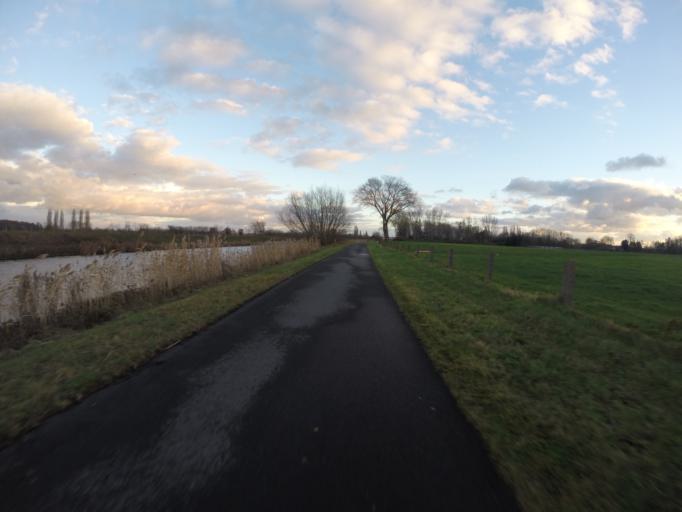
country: BE
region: Flanders
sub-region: Provincie Oost-Vlaanderen
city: Aalter
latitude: 51.1031
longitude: 3.4856
